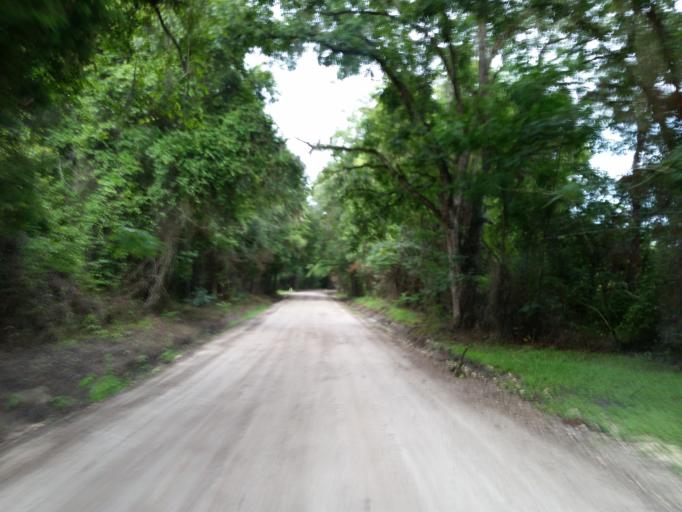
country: US
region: Florida
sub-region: Alachua County
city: High Springs
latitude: 29.9697
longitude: -82.5640
